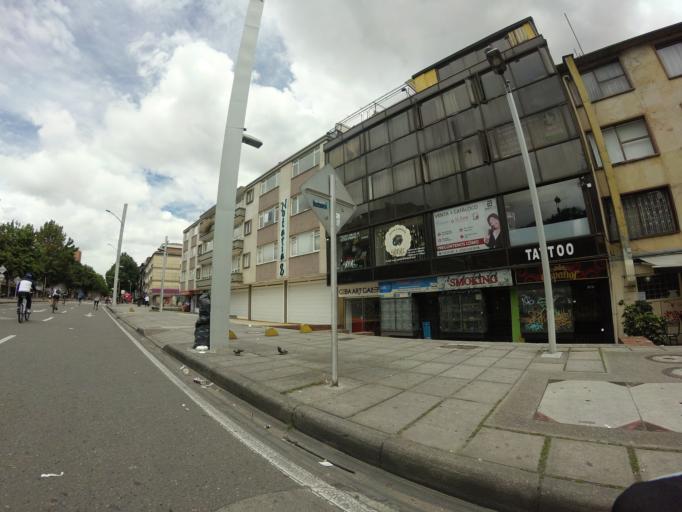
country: CO
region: Bogota D.C.
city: Barrio San Luis
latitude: 4.6679
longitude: -74.0564
